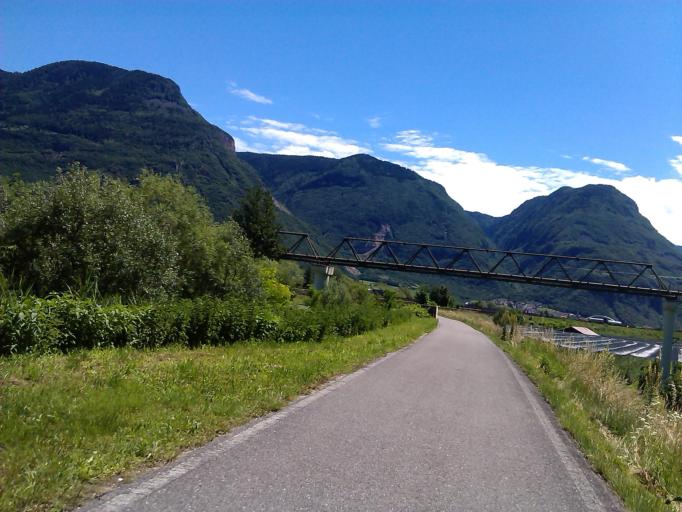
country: IT
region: Trentino-Alto Adige
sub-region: Bolzano
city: Vadena
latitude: 46.4235
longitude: 11.3107
